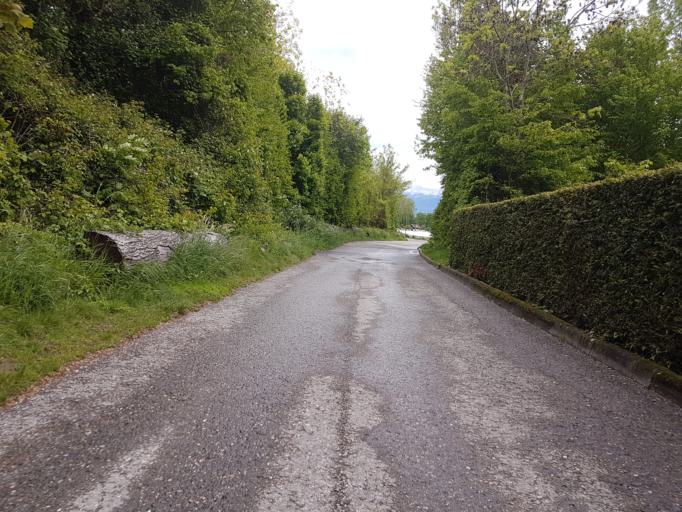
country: CH
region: Vaud
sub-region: Morges District
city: Preverenges
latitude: 46.5122
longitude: 6.5444
